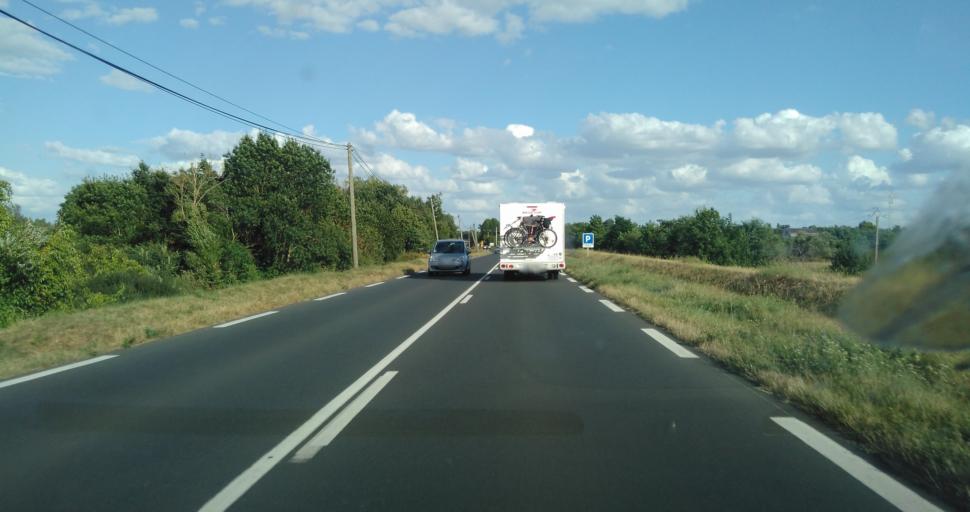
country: FR
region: Centre
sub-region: Departement d'Indre-et-Loire
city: Montlouis-sur-Loire
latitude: 47.4002
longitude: 0.8163
